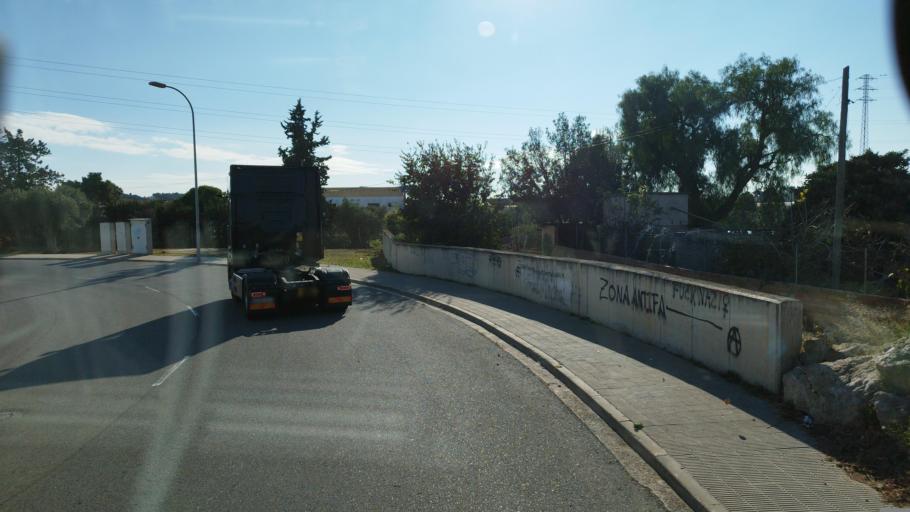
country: ES
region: Catalonia
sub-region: Provincia de Tarragona
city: Torredembarra
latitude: 41.1502
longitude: 1.3898
